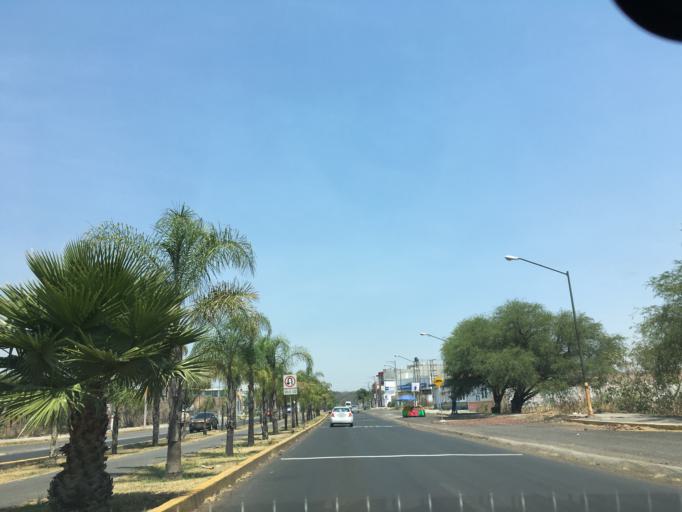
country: MX
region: Guanajuato
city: Moroleon
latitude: 20.1034
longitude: -101.1649
